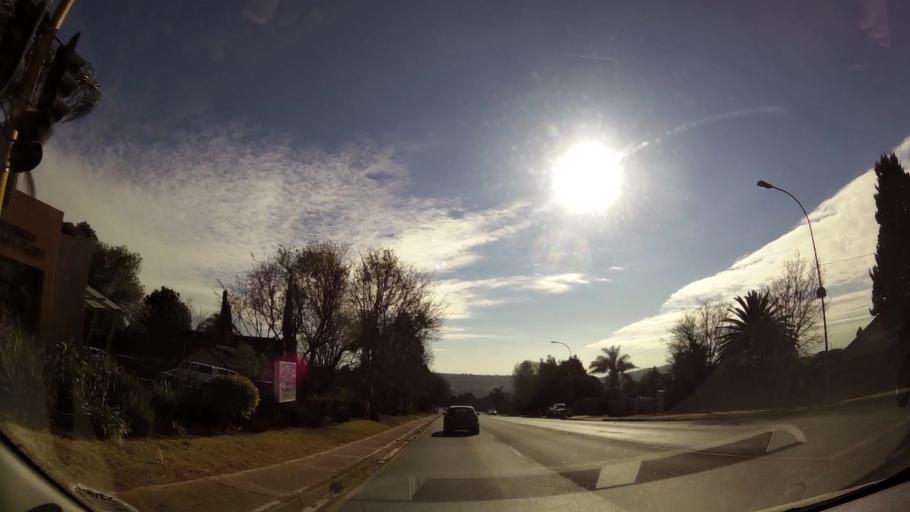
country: ZA
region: Gauteng
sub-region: City of Johannesburg Metropolitan Municipality
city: Roodepoort
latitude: -26.1218
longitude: 27.8495
